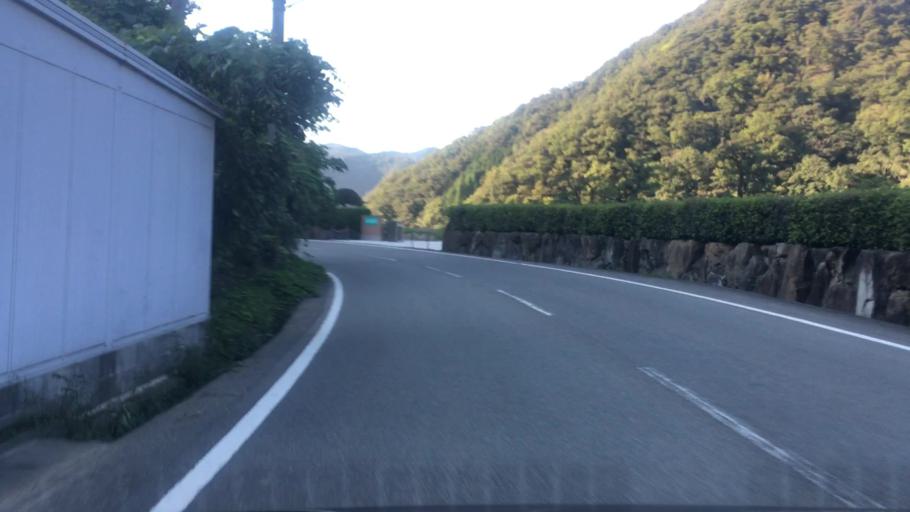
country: JP
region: Hyogo
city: Toyooka
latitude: 35.6157
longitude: 134.8263
